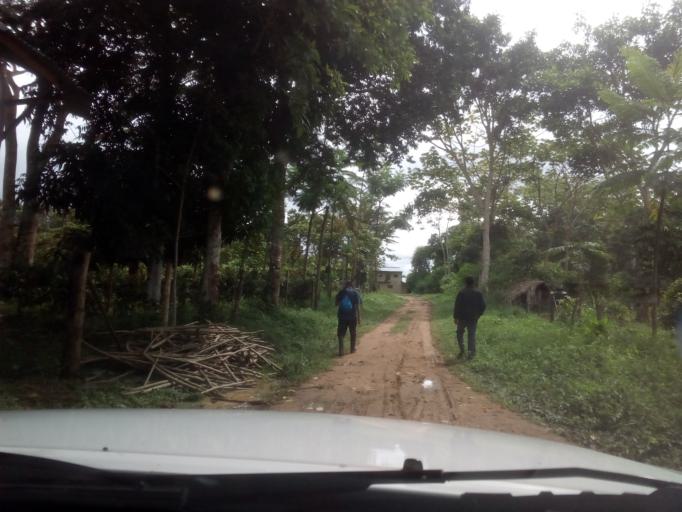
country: PE
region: San Martin
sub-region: Provincia de Lamas
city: Lamas
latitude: -6.4106
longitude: -76.4667
